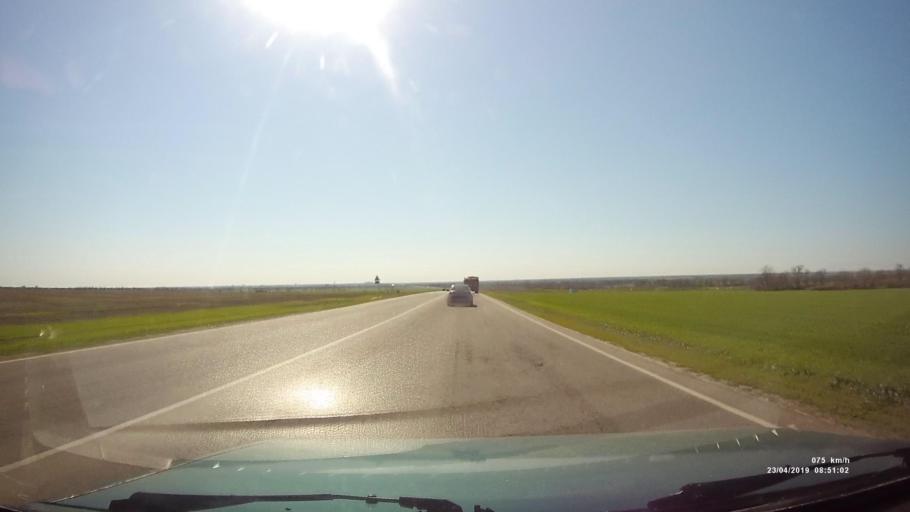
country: RU
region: Rostov
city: Gigant
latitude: 46.4918
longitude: 41.4373
